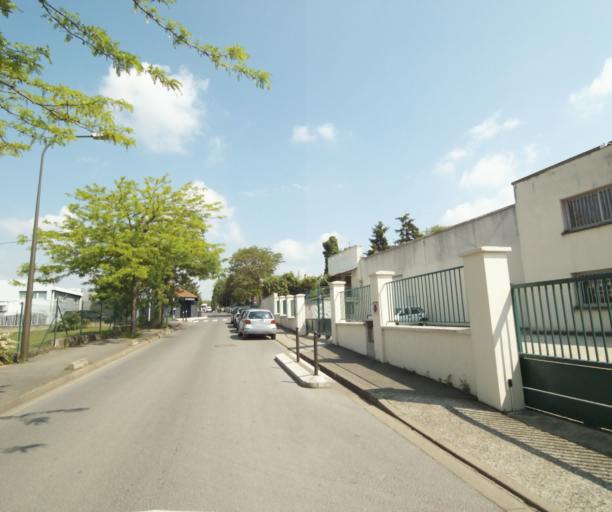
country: FR
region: Ile-de-France
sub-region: Departement des Yvelines
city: Sartrouville
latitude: 48.9466
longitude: 2.2099
